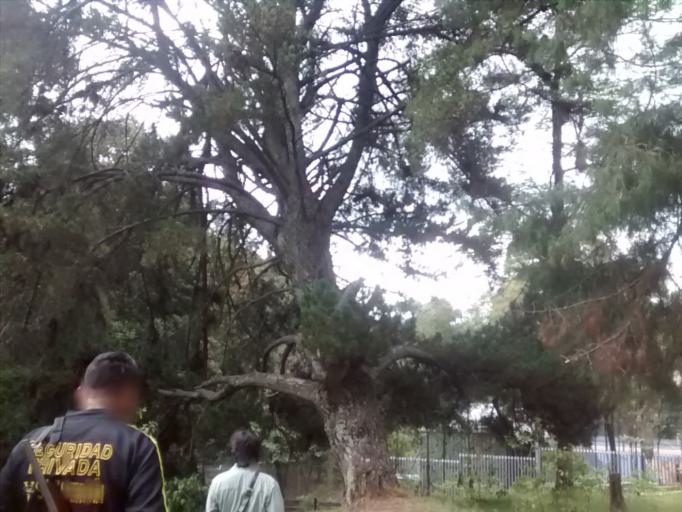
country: CO
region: Bogota D.C.
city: Bogota
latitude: 4.5992
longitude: -74.0629
